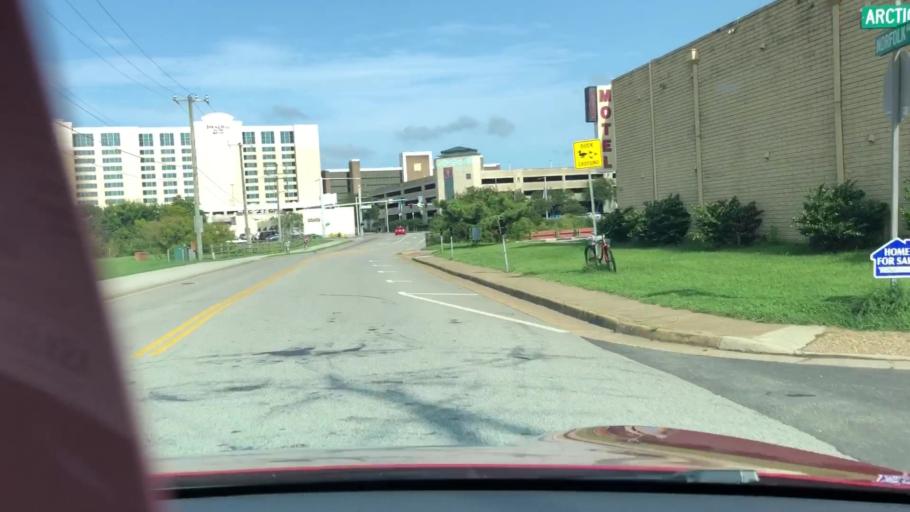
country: US
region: Virginia
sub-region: City of Virginia Beach
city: Virginia Beach
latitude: 36.8376
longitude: -75.9754
